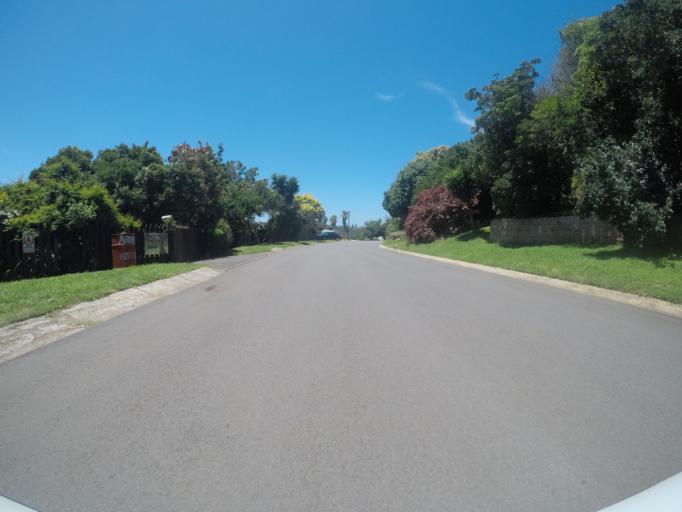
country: ZA
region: Eastern Cape
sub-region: Buffalo City Metropolitan Municipality
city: East London
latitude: -32.9332
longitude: 28.0089
